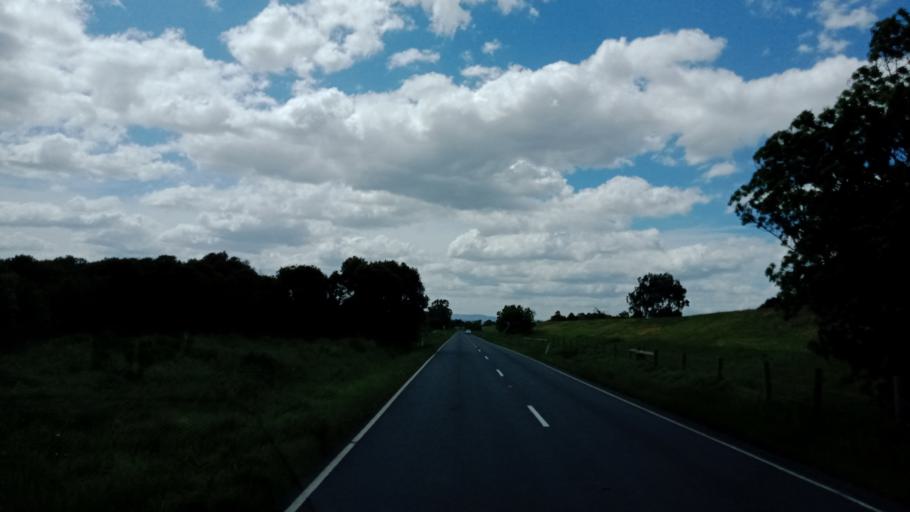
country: AU
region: Victoria
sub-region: Kingston
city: Chelsea Heights
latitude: -38.0409
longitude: 145.1758
